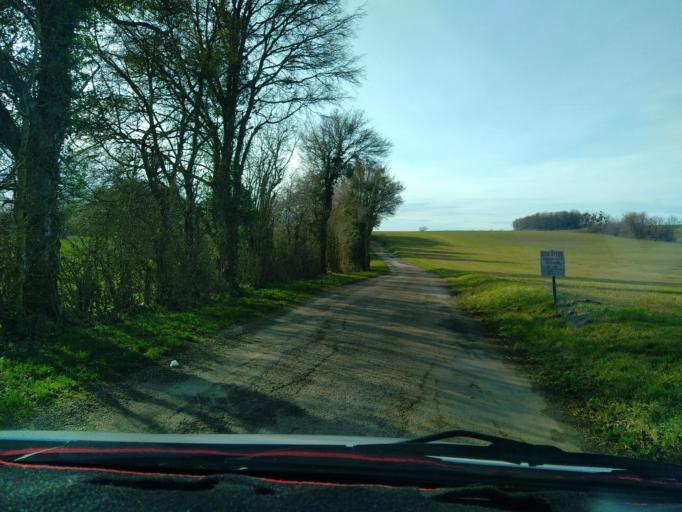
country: FR
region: Franche-Comte
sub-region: Departement de la Haute-Saone
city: Marnay
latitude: 47.3176
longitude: 5.6808
